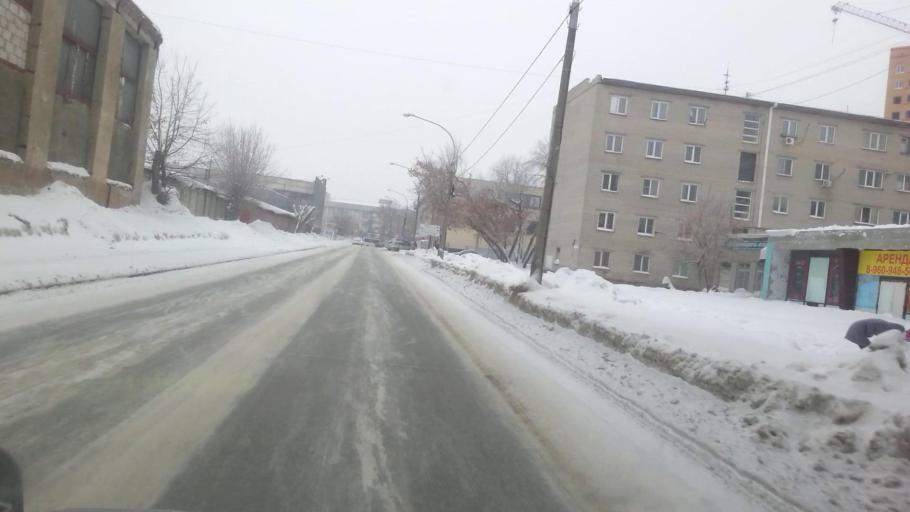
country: RU
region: Altai Krai
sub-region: Gorod Barnaulskiy
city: Barnaul
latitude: 53.3819
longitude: 83.7362
